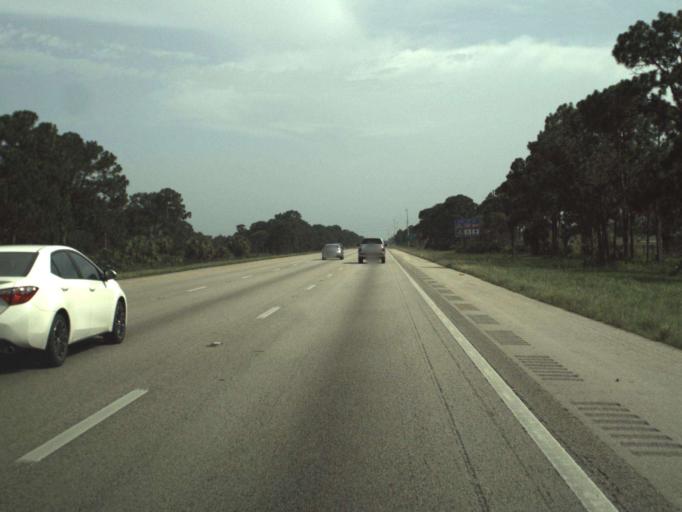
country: US
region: Florida
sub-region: Saint Lucie County
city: River Park
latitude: 27.3287
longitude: -80.4145
